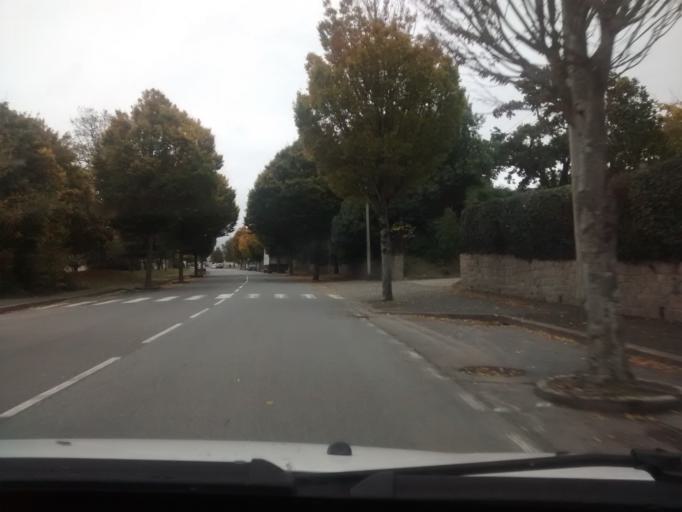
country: FR
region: Brittany
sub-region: Departement d'Ille-et-Vilaine
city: Dinard
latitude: 48.6292
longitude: -2.0754
